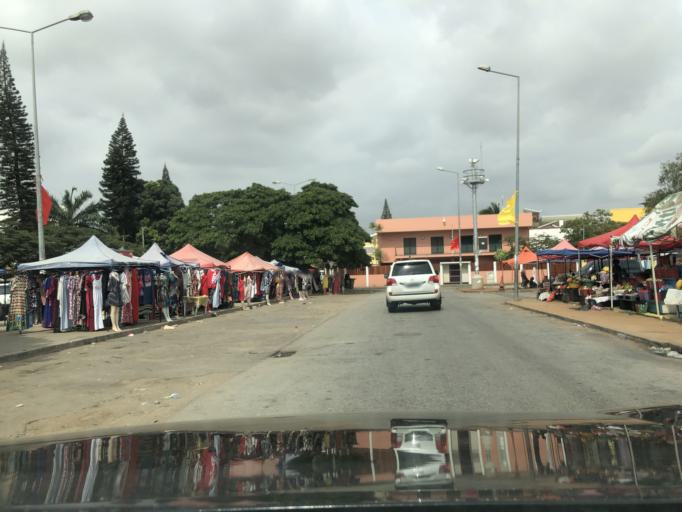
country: AO
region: Luanda
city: Luanda
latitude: -8.8285
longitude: 13.2477
